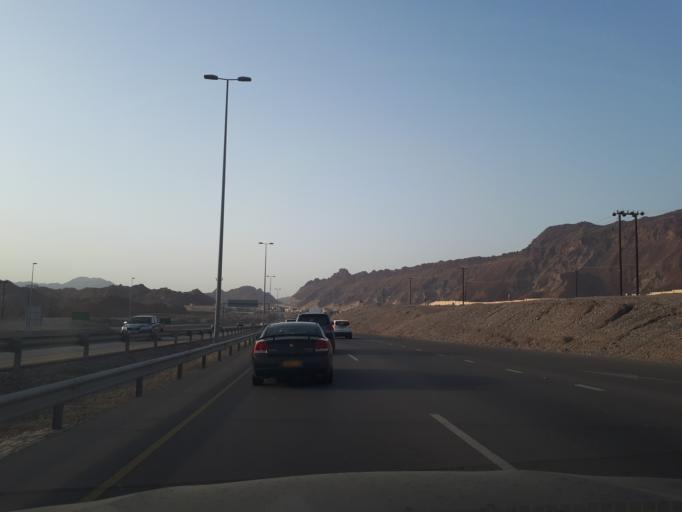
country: OM
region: Muhafazat ad Dakhiliyah
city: Bidbid
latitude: 23.4343
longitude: 58.1208
